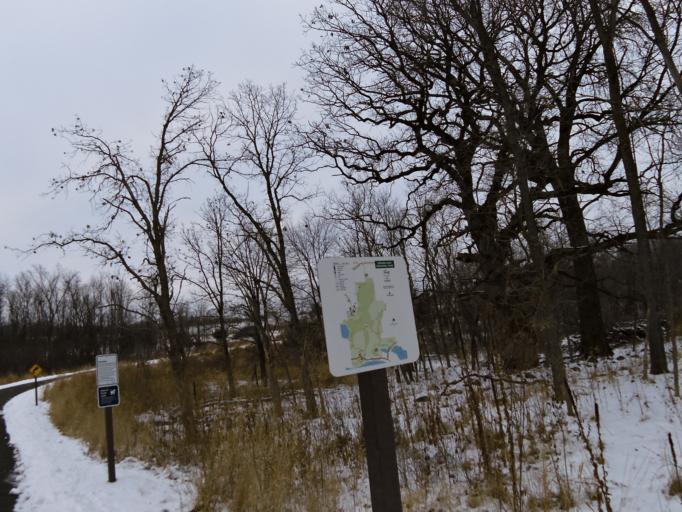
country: US
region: Minnesota
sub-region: Scott County
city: Prior Lake
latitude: 44.7078
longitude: -93.4727
